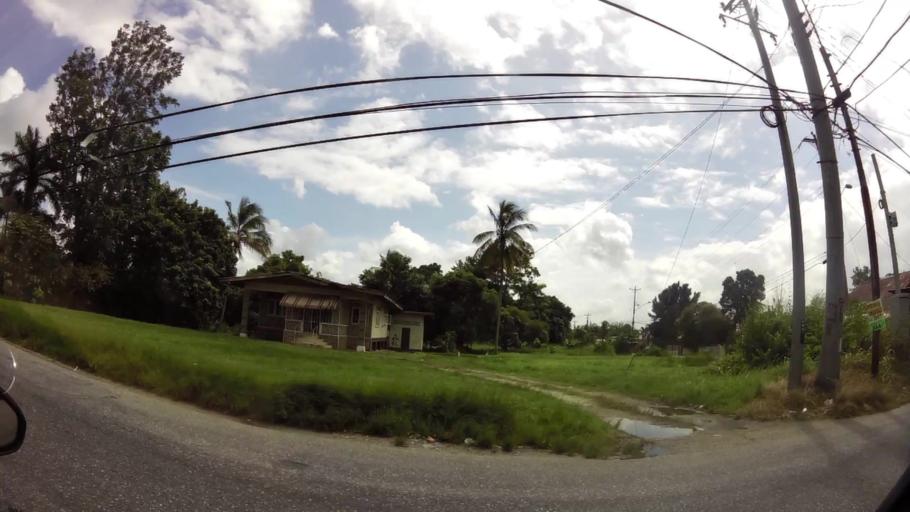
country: TT
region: Borough of Arima
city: Arima
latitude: 10.6348
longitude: -61.2912
